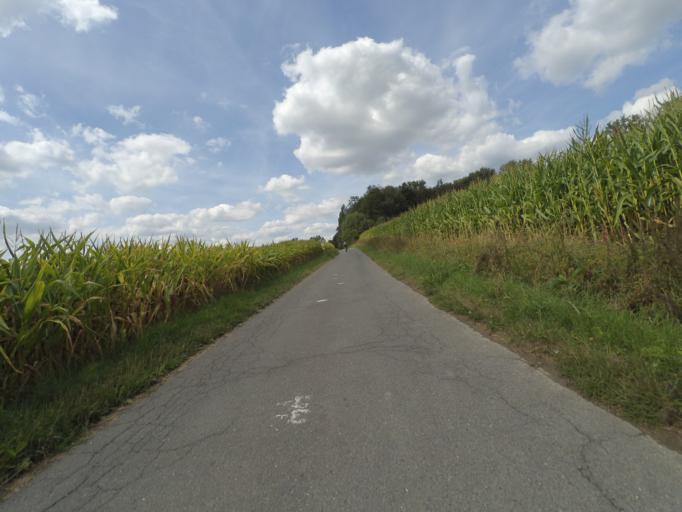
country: BE
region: Wallonia
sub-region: Province du Hainaut
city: Ellezelles
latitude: 50.8146
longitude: 3.6856
